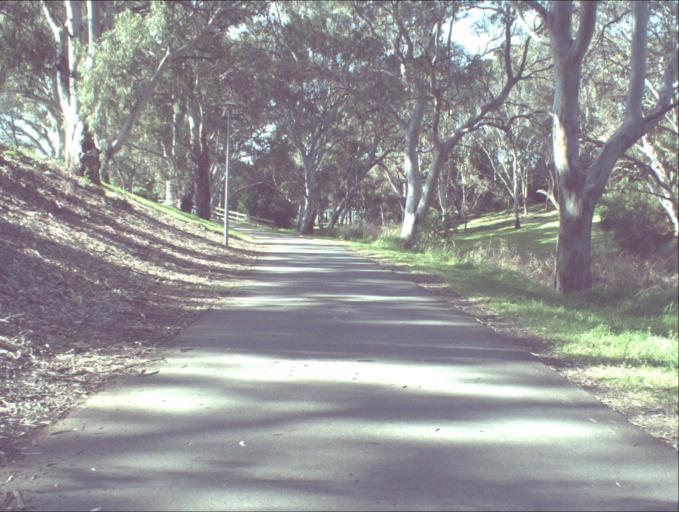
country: AU
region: South Australia
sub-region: Port Adelaide Enfield
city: Klemzig
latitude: -34.8822
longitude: 138.6477
